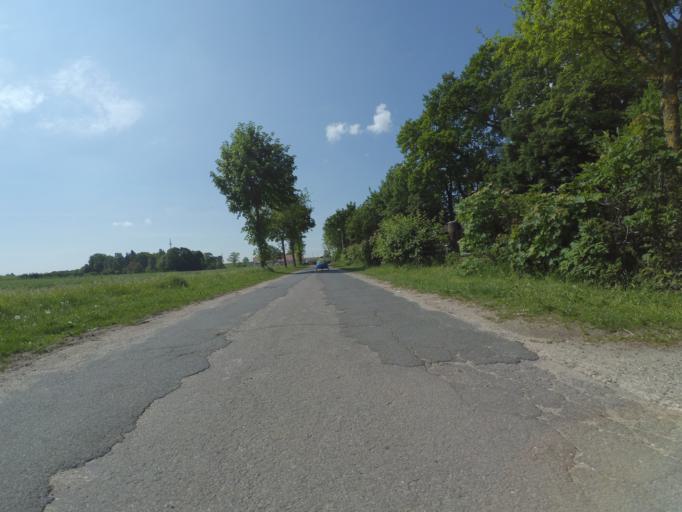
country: DE
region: Lower Saxony
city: Isernhagen Farster Bauerschaft
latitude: 52.5105
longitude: 9.9271
